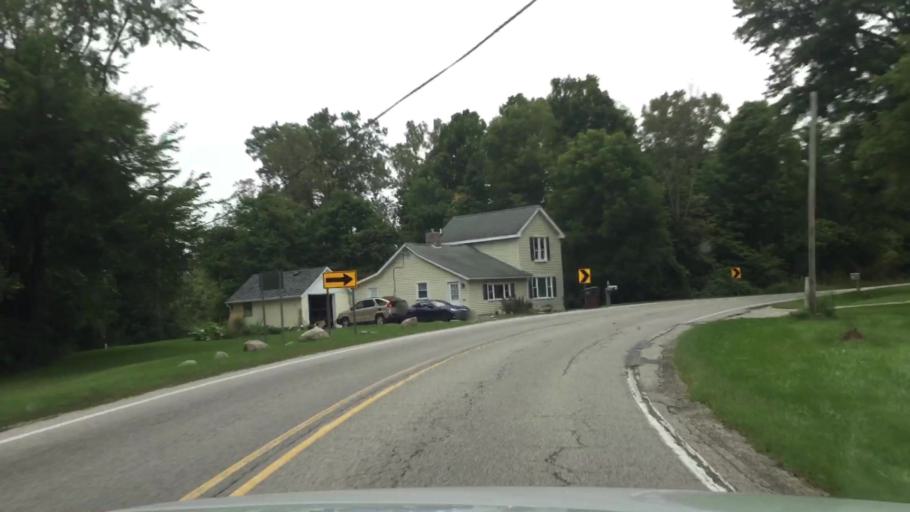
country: US
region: Michigan
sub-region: Washtenaw County
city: Milan
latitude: 42.1046
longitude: -83.7336
